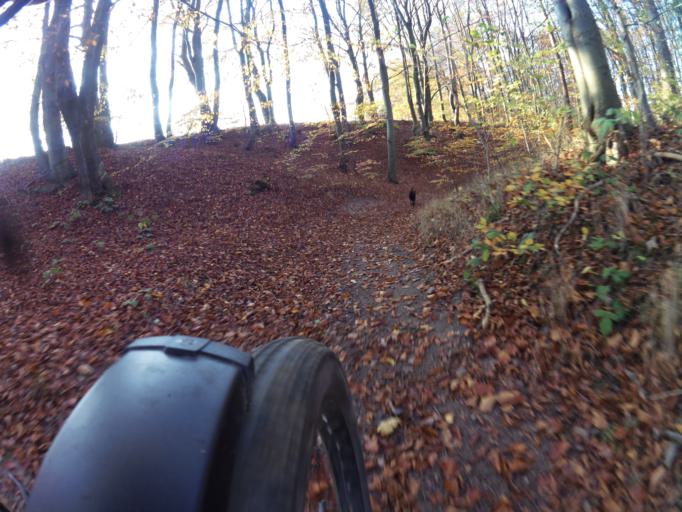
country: PL
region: Pomeranian Voivodeship
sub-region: Powiat pucki
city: Krokowa
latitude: 54.7699
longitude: 18.1770
